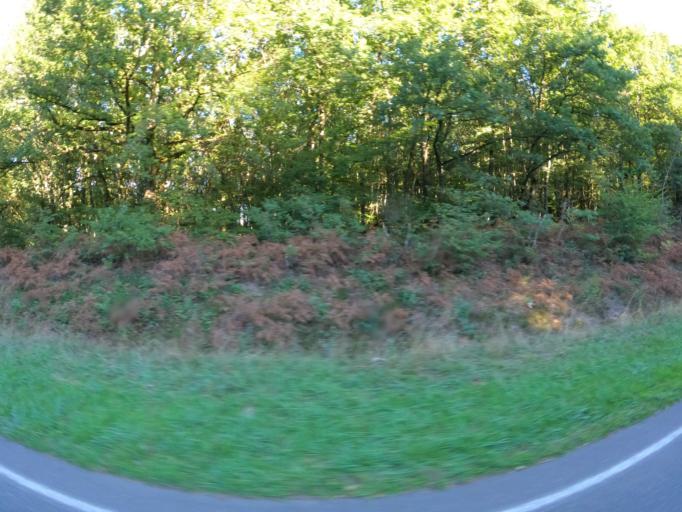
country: FR
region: Bourgogne
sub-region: Departement de Saone-et-Loire
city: Torcy
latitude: 46.7608
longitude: 4.4424
